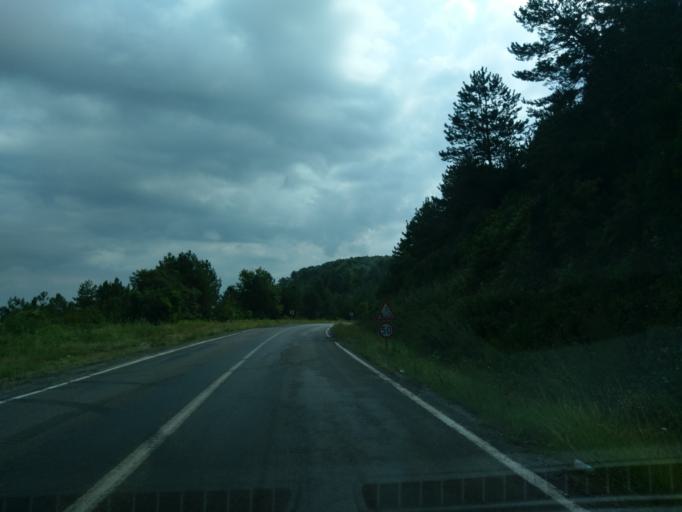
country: TR
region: Sinop
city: Yenikonak
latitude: 41.9428
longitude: 34.7025
